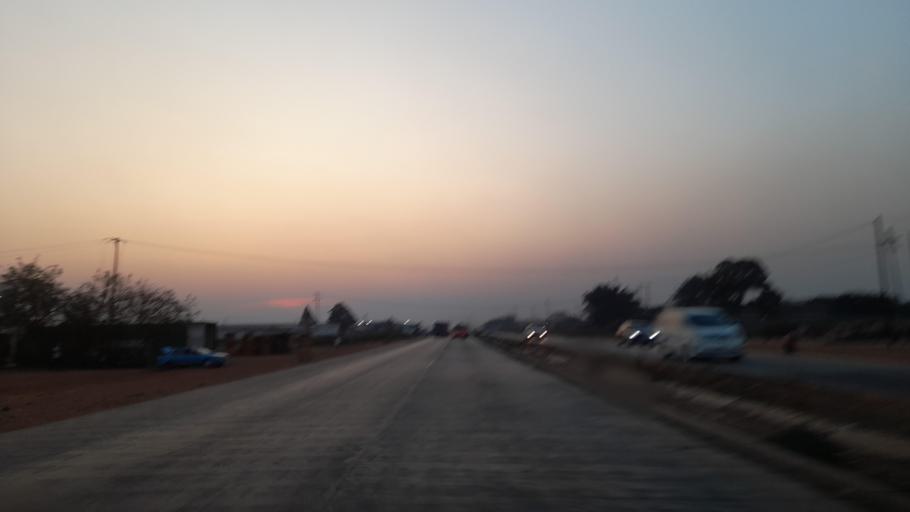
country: ZM
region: Copperbelt
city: Kitwe
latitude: -12.7724
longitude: 28.1860
